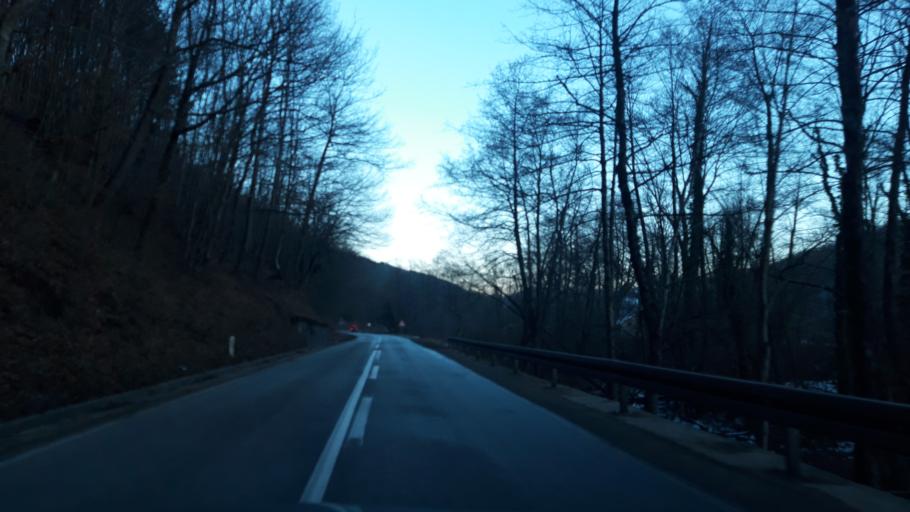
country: BA
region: Republika Srpska
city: Milici
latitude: 44.1691
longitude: 19.0276
